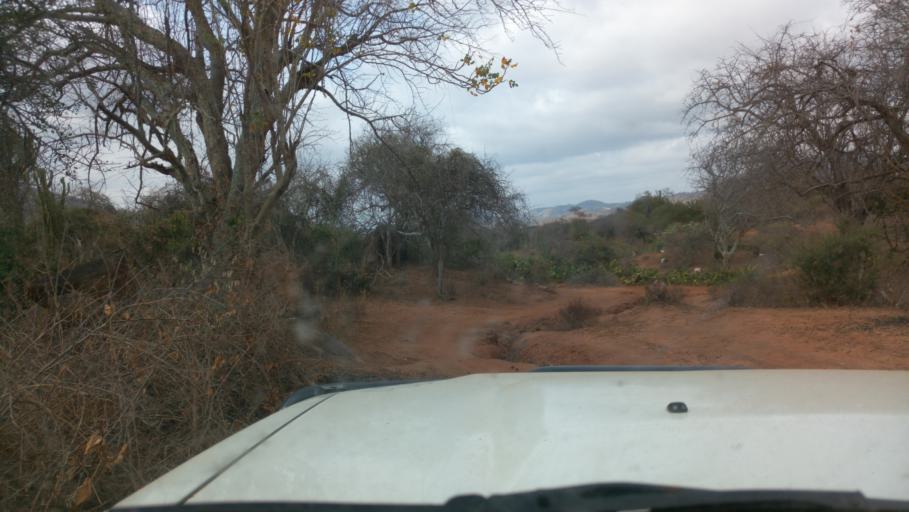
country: KE
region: Kitui
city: Kitui
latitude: -1.8634
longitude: 38.2809
